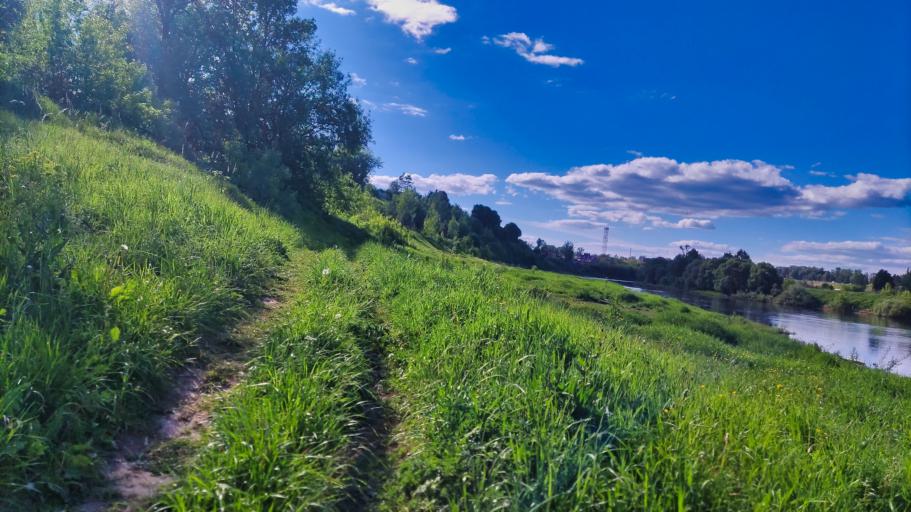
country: RU
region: Tverskaya
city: Rzhev
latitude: 56.2513
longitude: 34.3470
